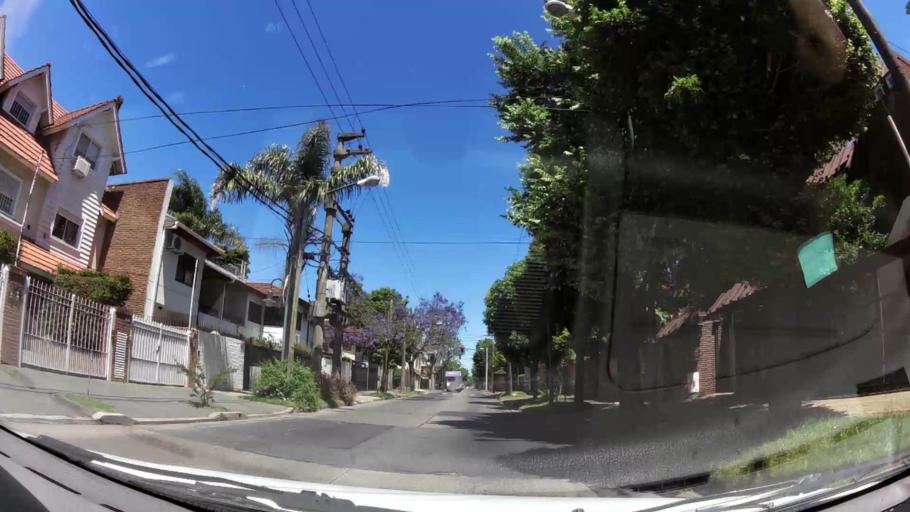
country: AR
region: Buenos Aires
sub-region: Partido de Vicente Lopez
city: Olivos
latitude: -34.5047
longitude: -58.5128
